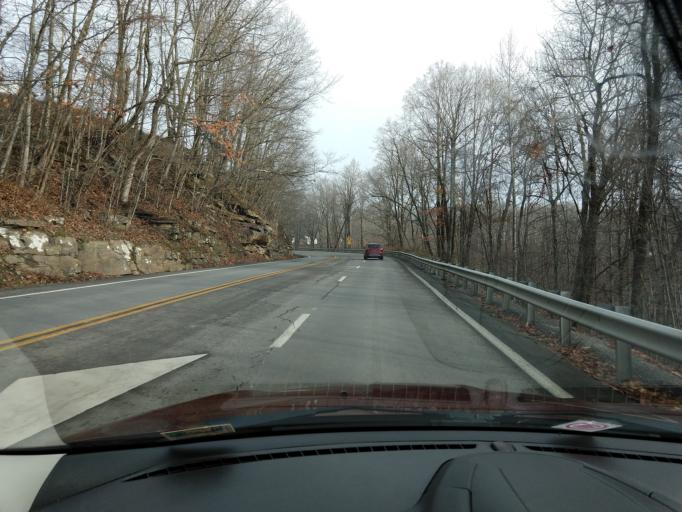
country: US
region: West Virginia
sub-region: Greenbrier County
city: Rainelle
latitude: 38.0238
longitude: -80.7257
